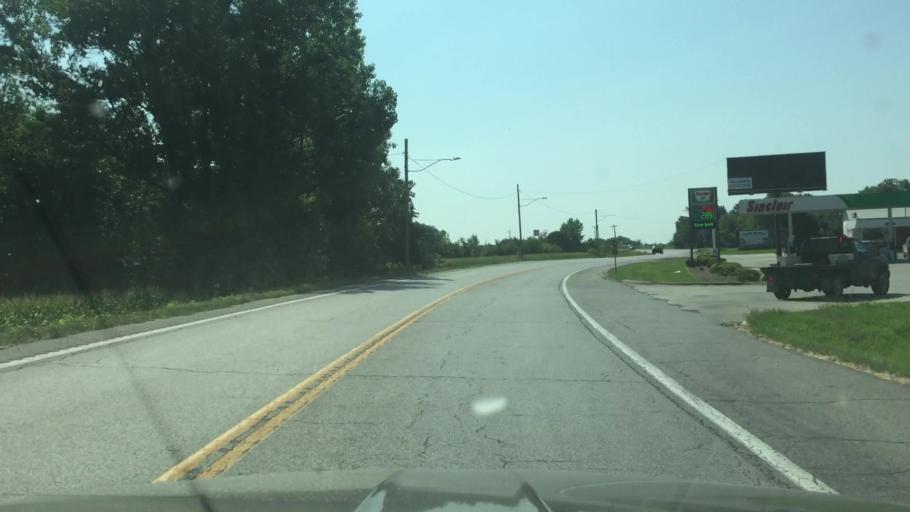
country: US
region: Missouri
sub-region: Pettis County
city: Sedalia
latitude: 38.6992
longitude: -93.1840
